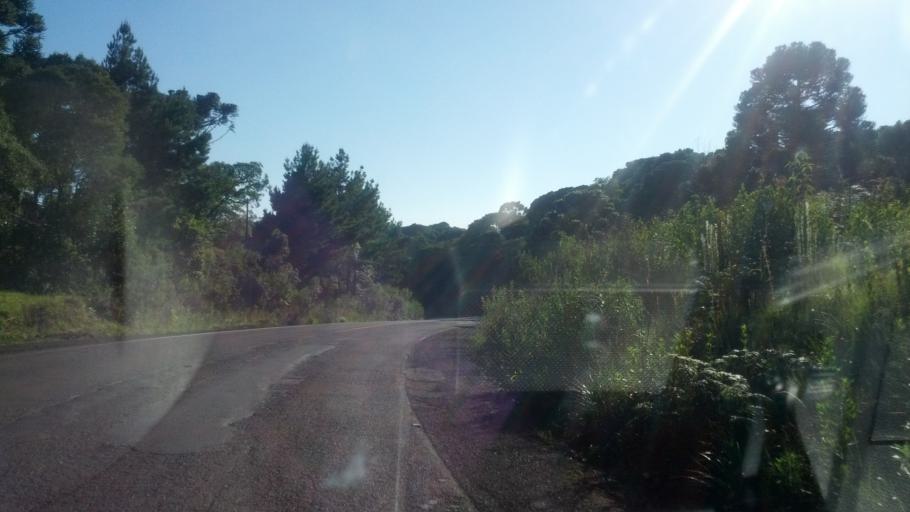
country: BR
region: Santa Catarina
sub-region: Lages
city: Lages
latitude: -27.9268
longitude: -50.5497
